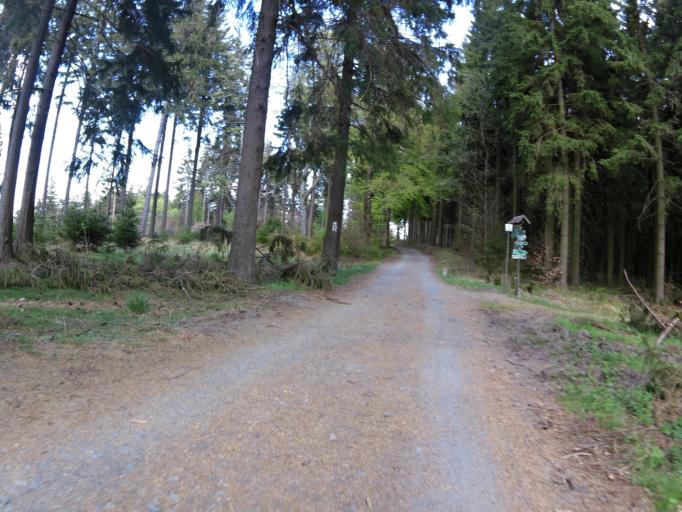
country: DE
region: Thuringia
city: Pappenheim
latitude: 50.7833
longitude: 10.5422
